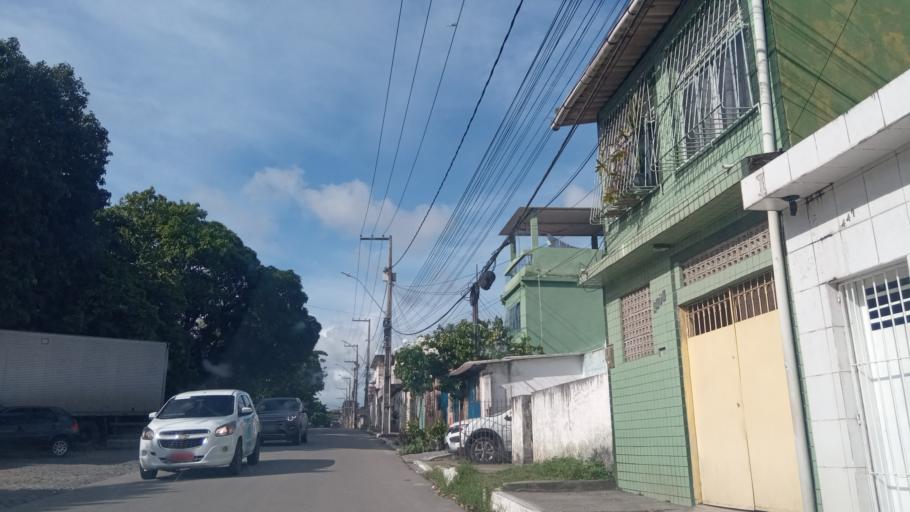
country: BR
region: Pernambuco
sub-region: Jaboatao Dos Guararapes
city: Jaboatao dos Guararapes
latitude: -8.1340
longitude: -34.9520
